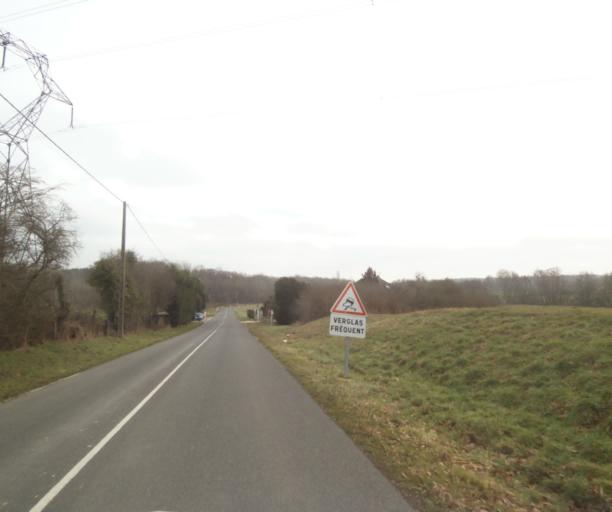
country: FR
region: Champagne-Ardenne
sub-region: Departement de la Marne
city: Pargny-sur-Saulx
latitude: 48.7488
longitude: 4.8577
